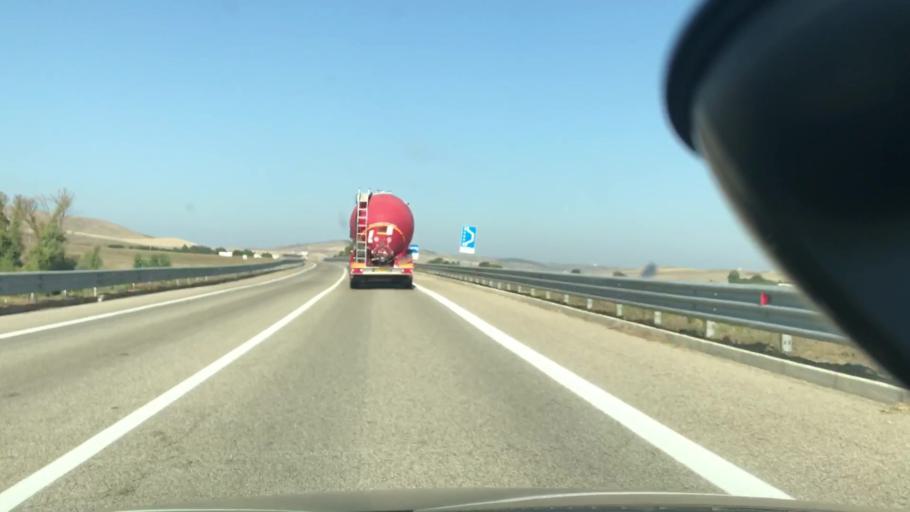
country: IT
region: Basilicate
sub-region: Provincia di Matera
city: Irsina
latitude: 40.7815
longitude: 16.3109
